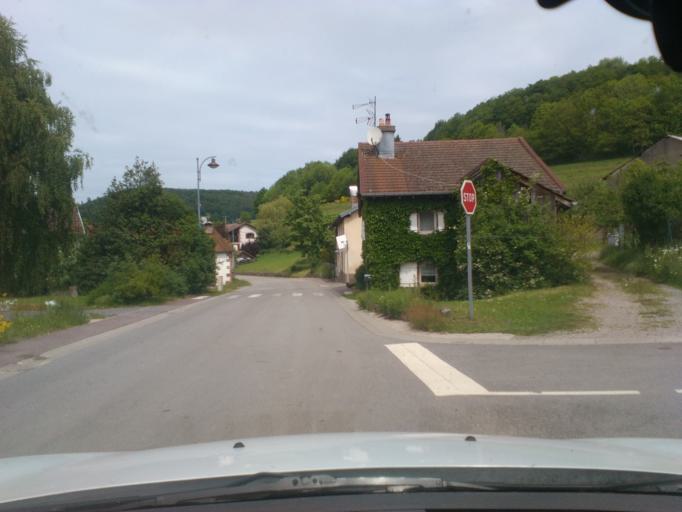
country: FR
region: Lorraine
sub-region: Departement des Vosges
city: Le Tholy
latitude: 48.1354
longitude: 6.7044
